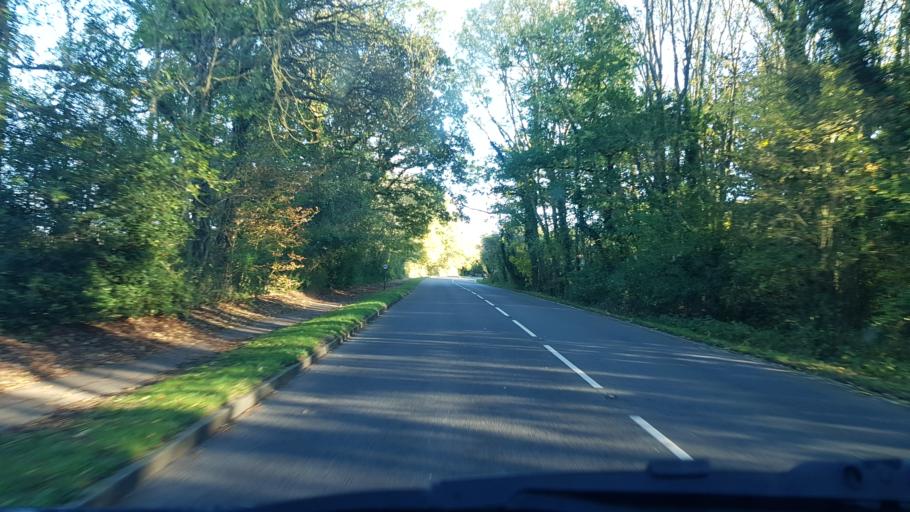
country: GB
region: England
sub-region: Surrey
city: Guildford
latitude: 51.2576
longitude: -0.6107
